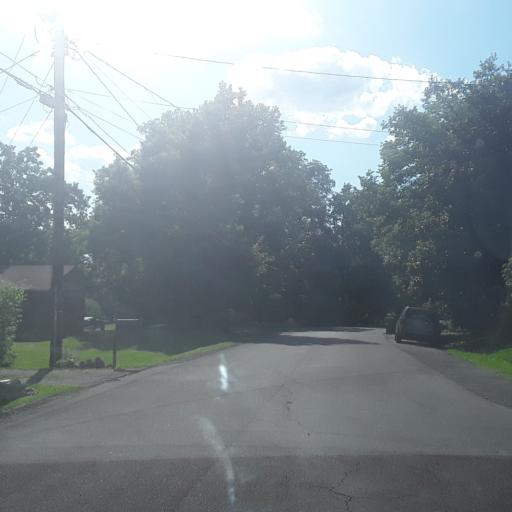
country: US
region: Tennessee
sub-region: Davidson County
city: Lakewood
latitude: 36.2027
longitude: -86.6318
